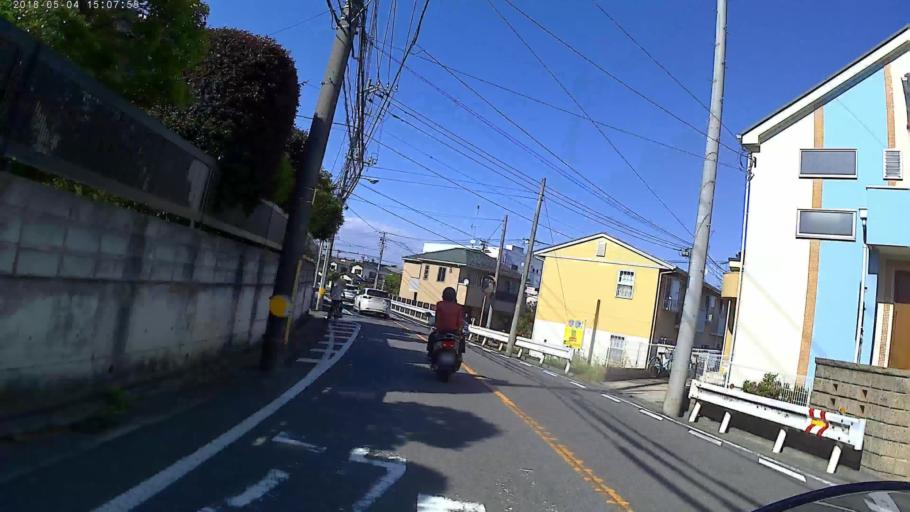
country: JP
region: Kanagawa
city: Yokohama
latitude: 35.5162
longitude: 139.6098
